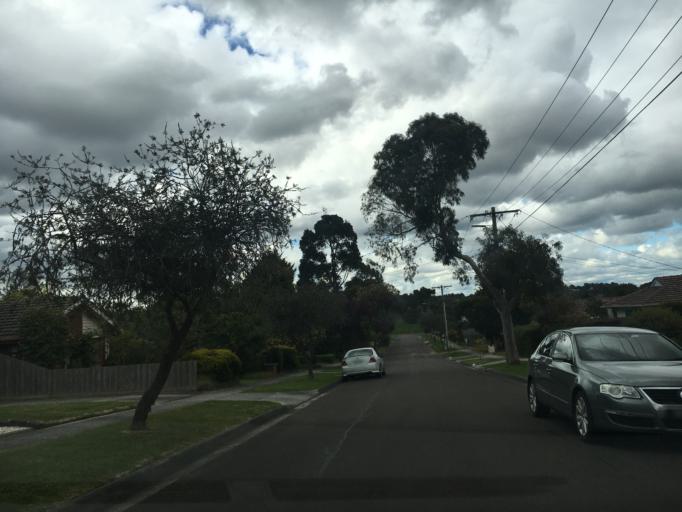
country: AU
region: Victoria
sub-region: Whitehorse
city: Vermont South
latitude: -37.8734
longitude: 145.1770
